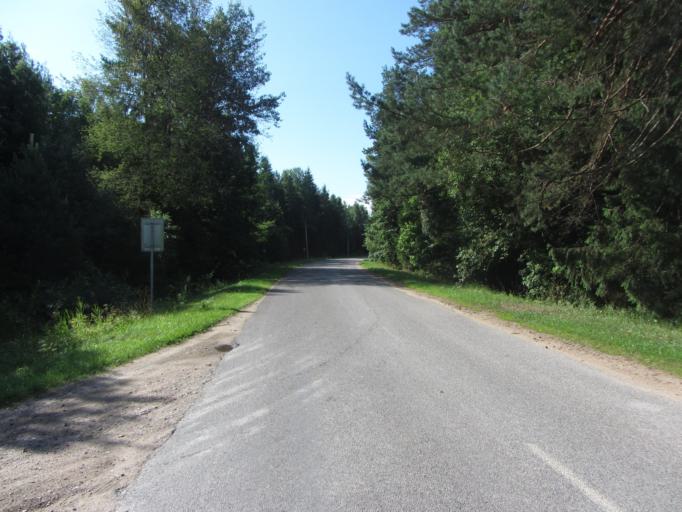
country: LT
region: Vilnius County
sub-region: Vilniaus Rajonas
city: Vievis
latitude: 54.8235
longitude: 24.8308
